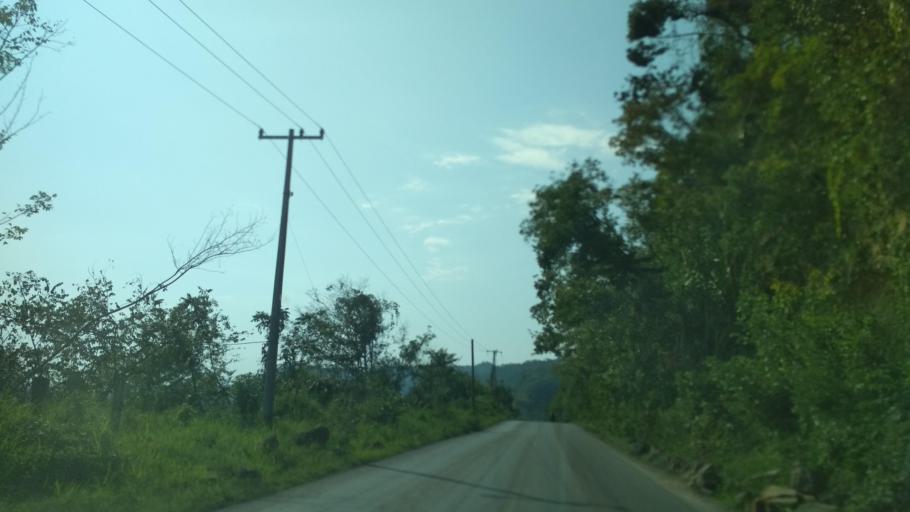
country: MX
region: Veracruz
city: Agua Dulce
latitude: 20.3992
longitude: -97.2417
